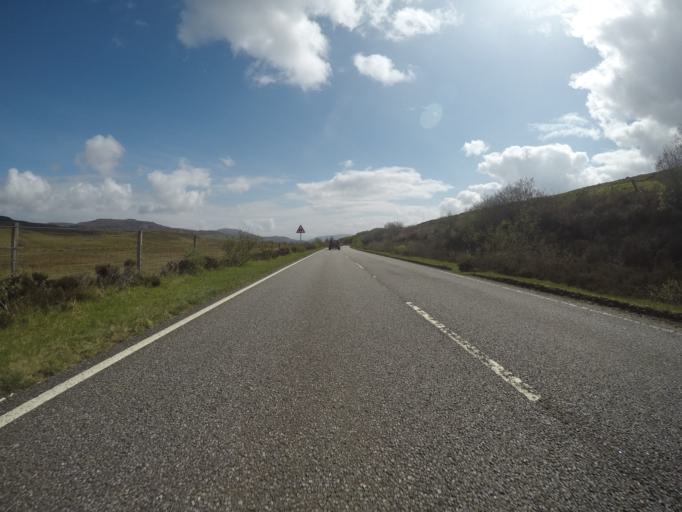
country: GB
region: Scotland
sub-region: Highland
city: Isle of Skye
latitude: 57.5079
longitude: -6.3367
